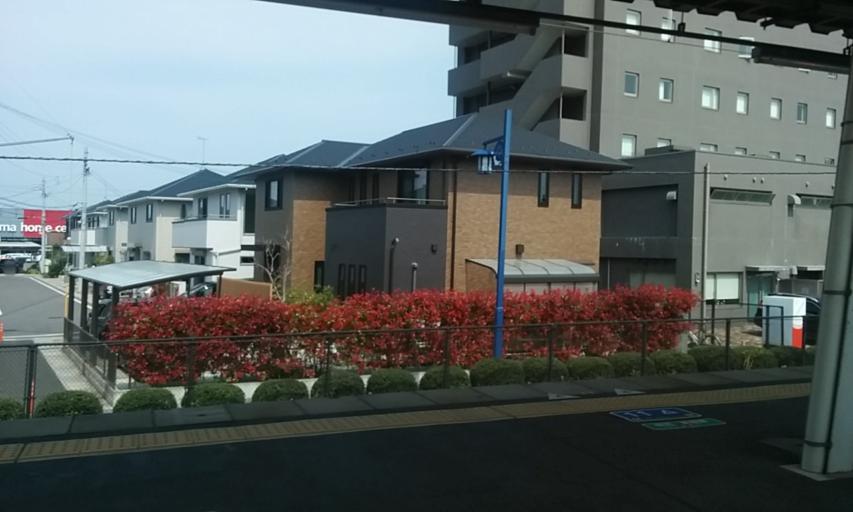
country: JP
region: Shiga Prefecture
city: Youkaichi
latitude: 35.1793
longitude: 136.1652
